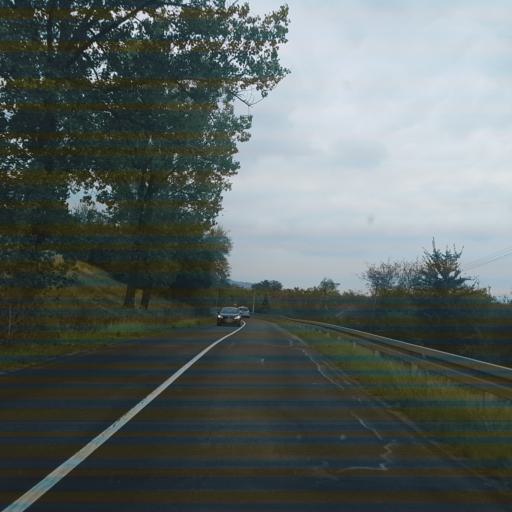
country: RS
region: Central Serbia
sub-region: Nisavski Okrug
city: Aleksinac
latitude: 43.5788
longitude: 21.6623
